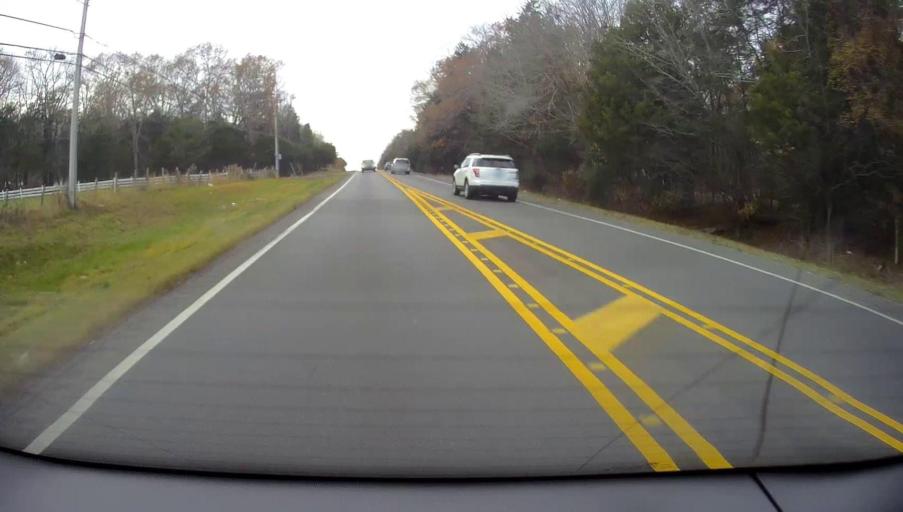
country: US
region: Alabama
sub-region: Morgan County
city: Priceville
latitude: 34.5144
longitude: -86.8804
